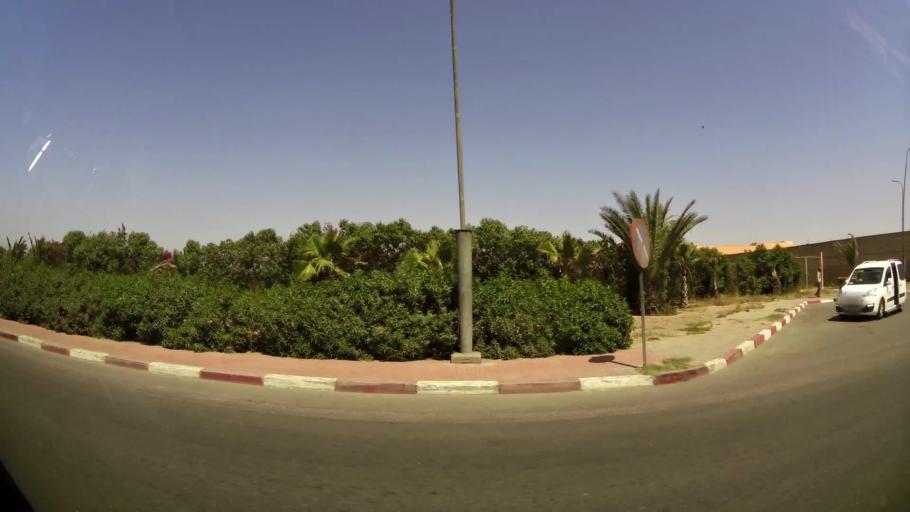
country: MA
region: Souss-Massa-Draa
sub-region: Inezgane-Ait Mellou
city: Inezgane
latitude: 30.3498
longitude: -9.5035
